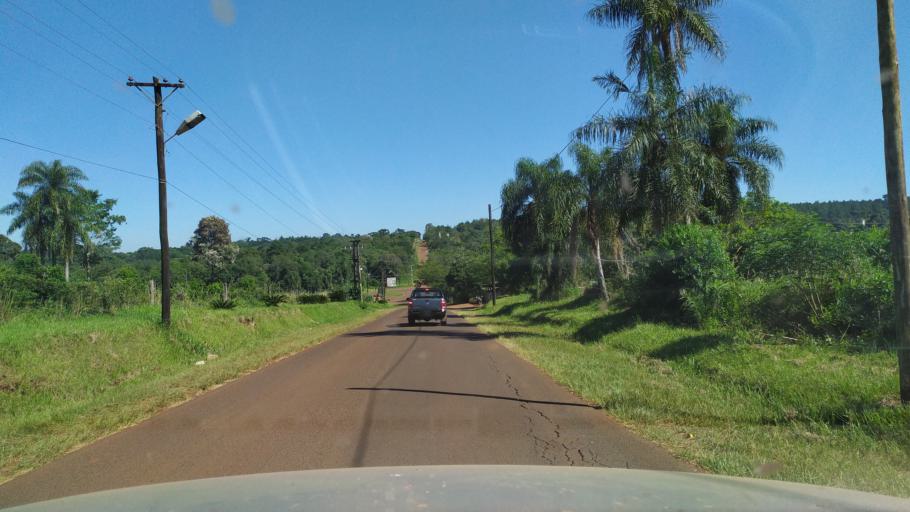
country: AR
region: Misiones
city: Caraguatay
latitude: -26.6442
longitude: -54.7509
